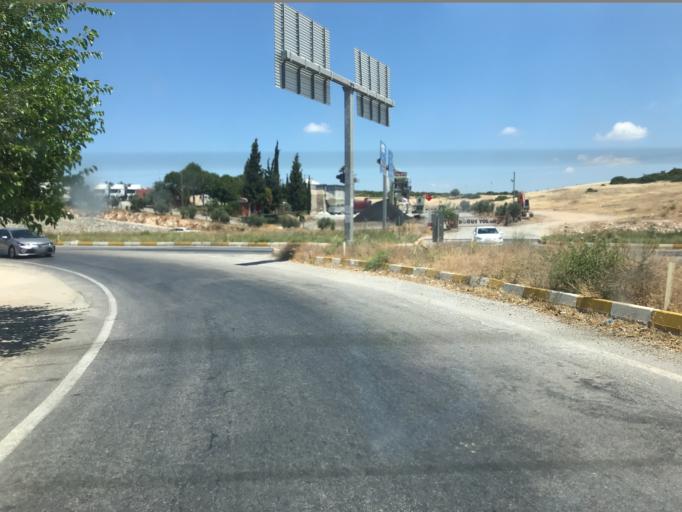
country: TR
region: Aydin
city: Akkoy
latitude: 37.4780
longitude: 27.3412
